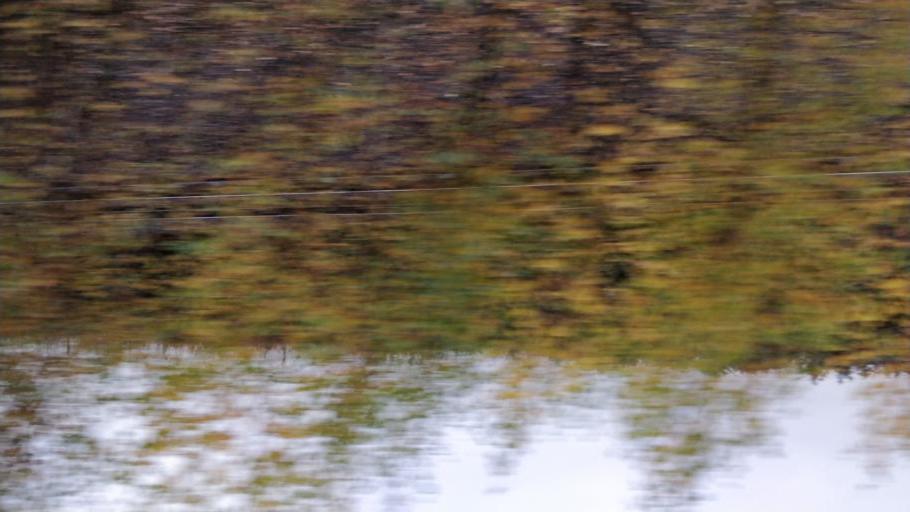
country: GB
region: England
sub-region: Borough of Wigan
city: Hindley
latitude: 53.5437
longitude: -2.5621
